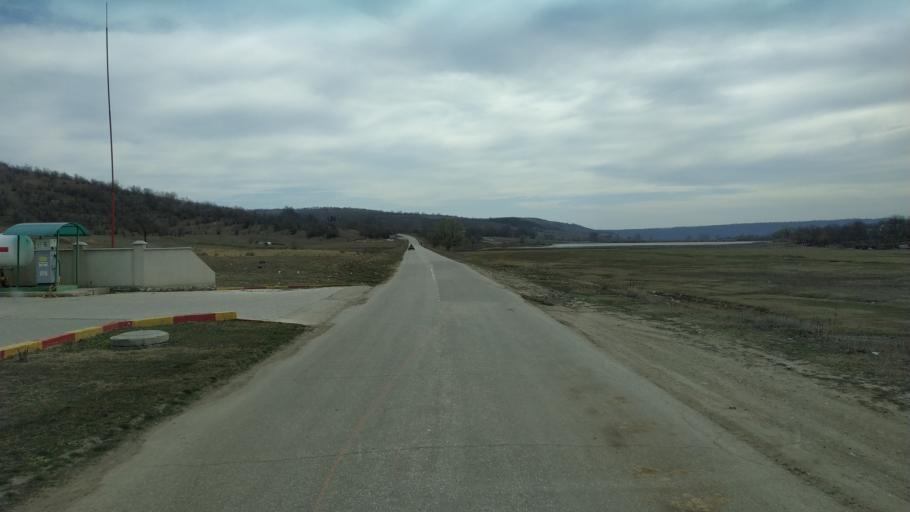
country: MD
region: Nisporeni
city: Nisporeni
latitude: 46.9601
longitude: 28.2182
